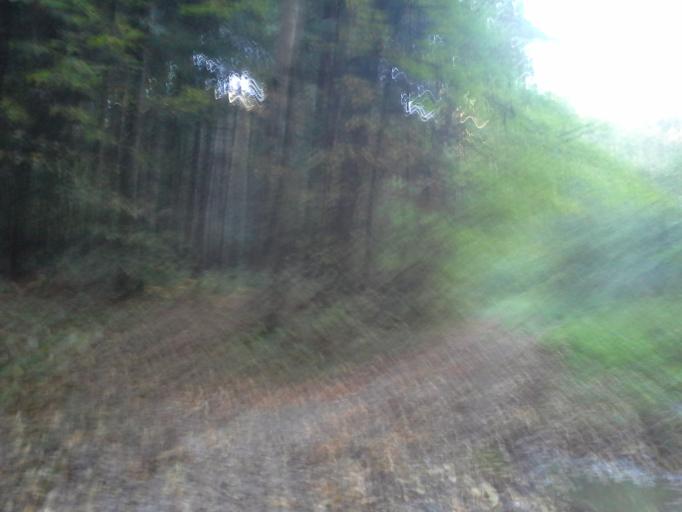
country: RU
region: Moskovskaya
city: Annino
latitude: 55.5531
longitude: 37.2733
